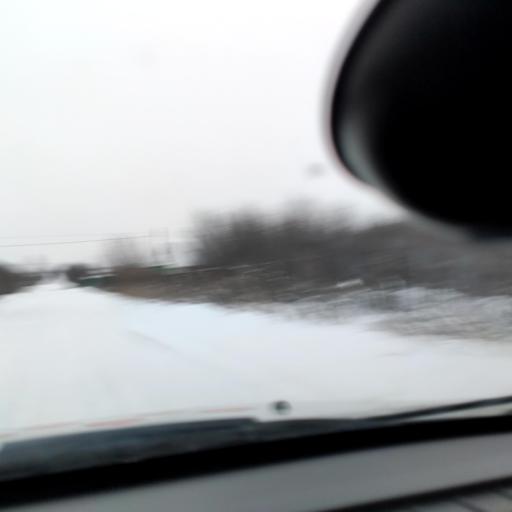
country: RU
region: Bashkortostan
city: Avdon
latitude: 54.5721
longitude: 55.7371
